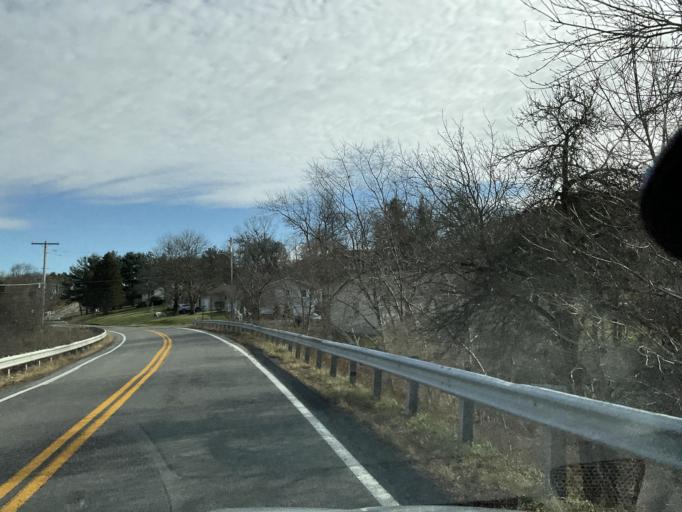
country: US
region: Maryland
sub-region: Garrett County
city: Oakland
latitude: 39.4065
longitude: -79.3967
